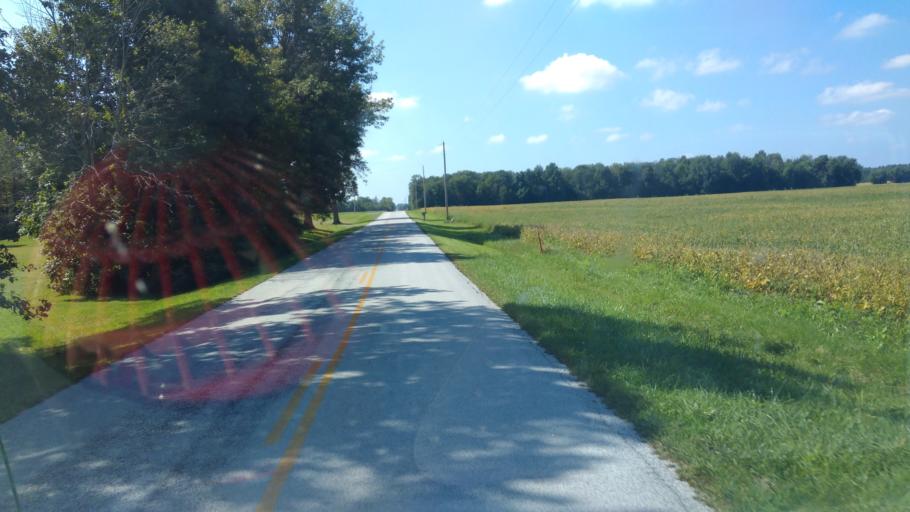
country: US
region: Ohio
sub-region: Hardin County
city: Ada
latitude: 40.7468
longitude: -83.7120
